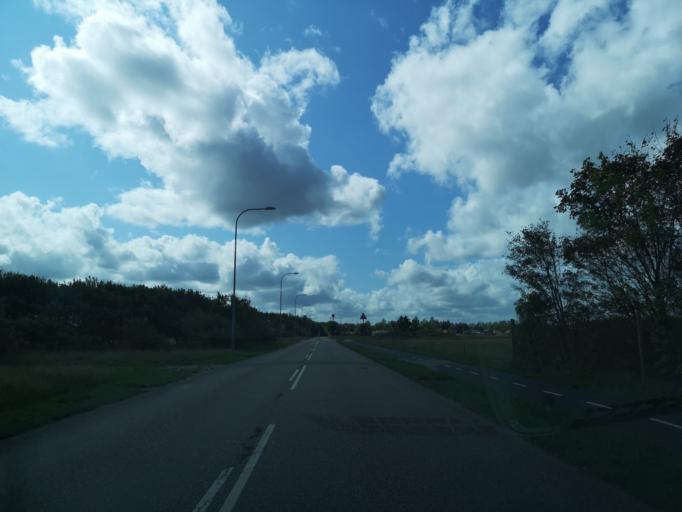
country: DK
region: Central Jutland
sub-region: Holstebro Kommune
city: Holstebro
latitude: 56.3843
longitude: 8.5767
